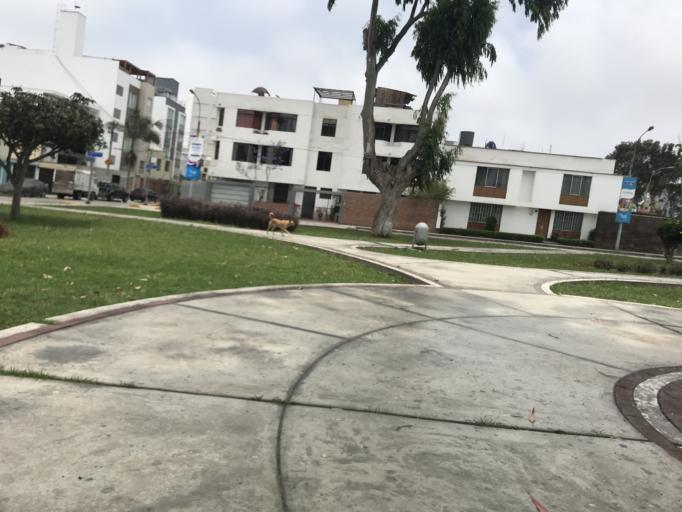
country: PE
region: Lima
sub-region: Lima
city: San Isidro
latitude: -12.0809
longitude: -77.0772
